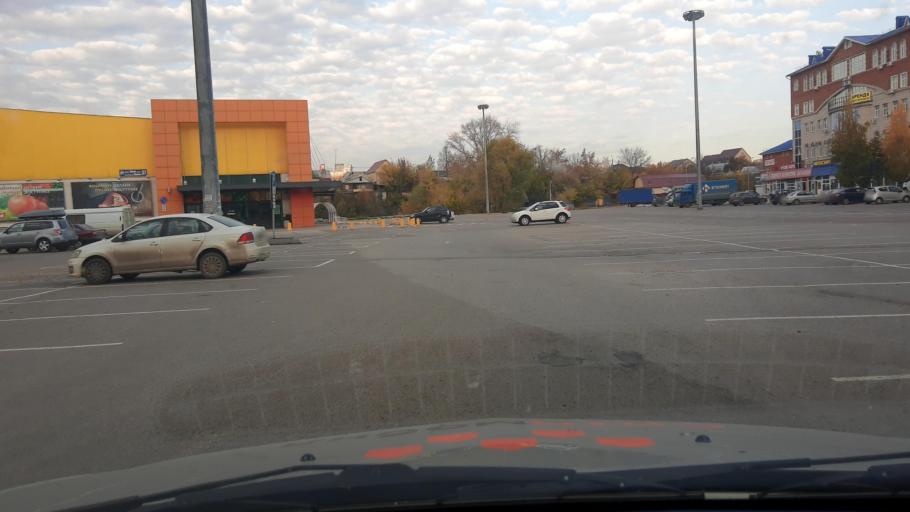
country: RU
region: Bashkortostan
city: Ufa
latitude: 54.7782
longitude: 56.0689
